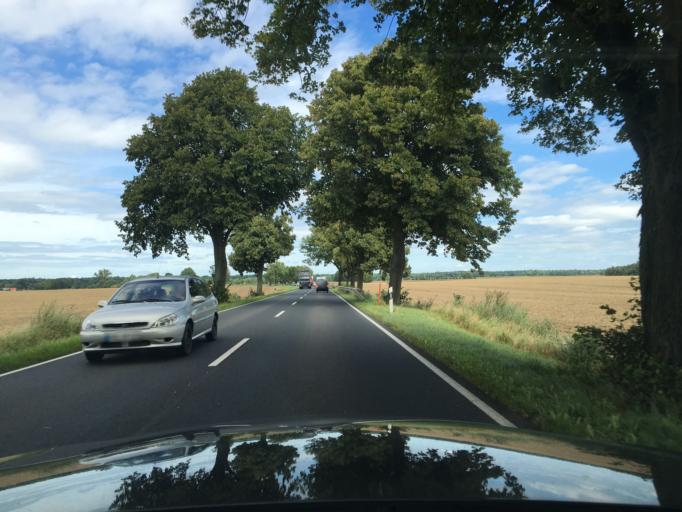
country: DE
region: Brandenburg
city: Gransee
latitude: 53.0436
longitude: 13.1946
